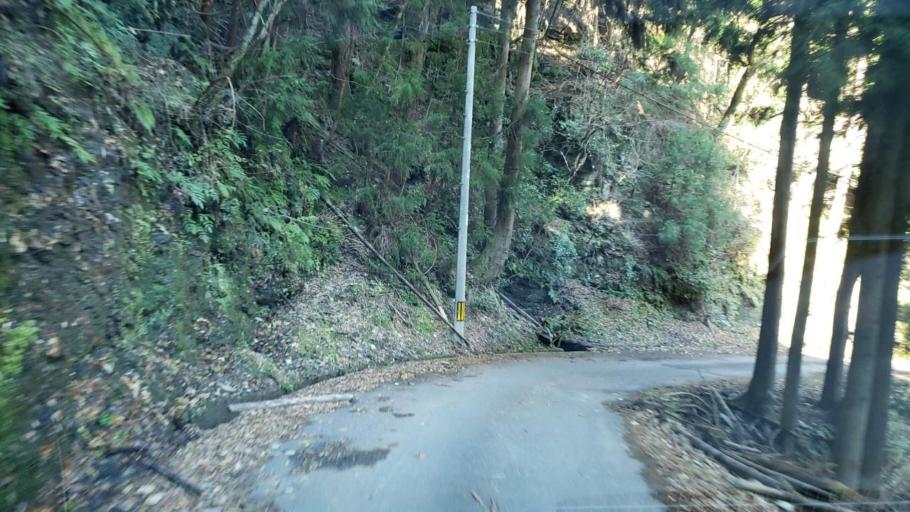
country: JP
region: Tokushima
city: Wakimachi
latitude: 33.9884
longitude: 133.9857
